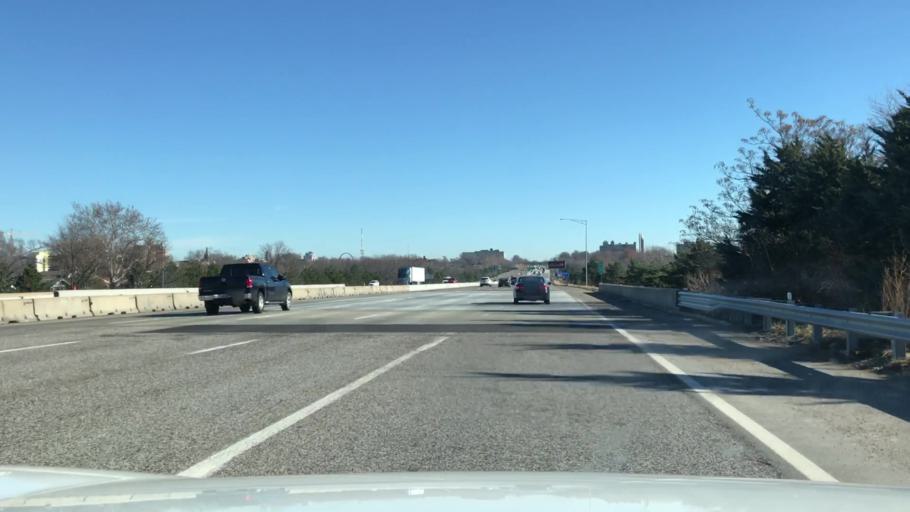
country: US
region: Missouri
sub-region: City of Saint Louis
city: St. Louis
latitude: 38.6181
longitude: -90.2567
